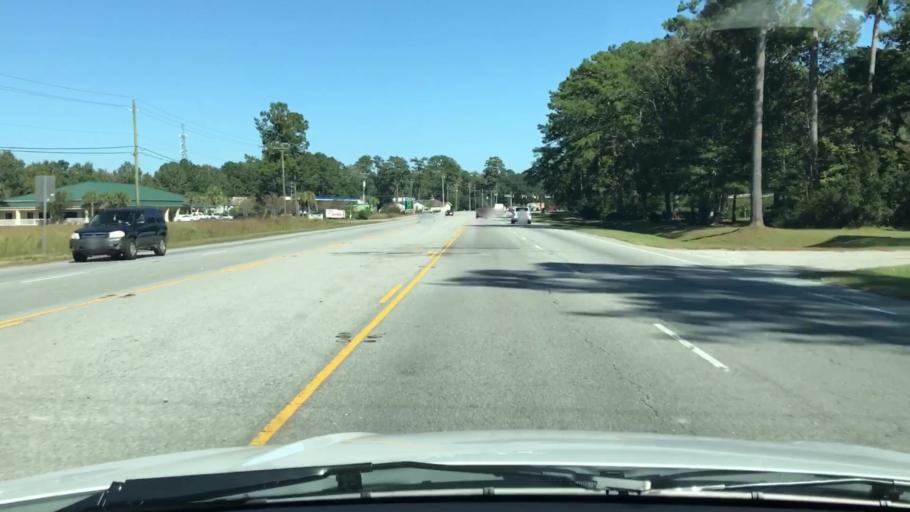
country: US
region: South Carolina
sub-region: Beaufort County
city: Laurel Bay
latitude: 32.3613
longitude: -80.8717
